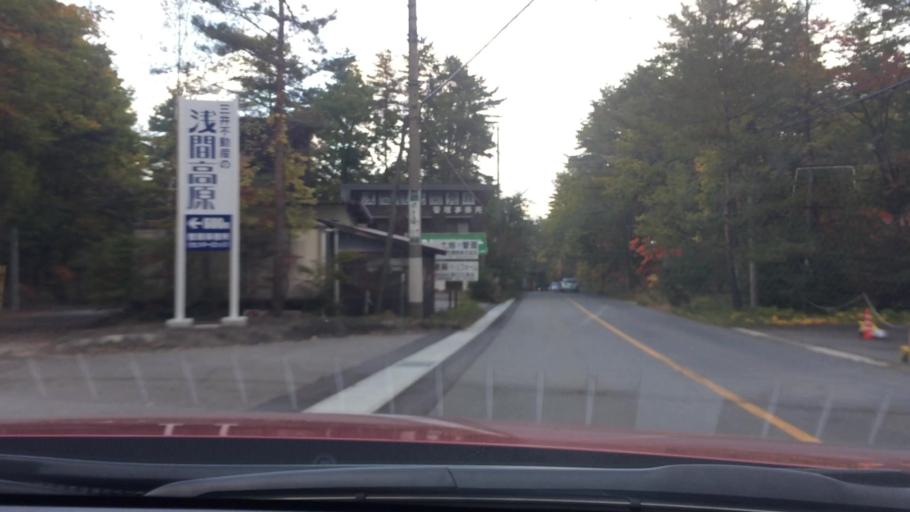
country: JP
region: Nagano
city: Komoro
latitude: 36.4393
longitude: 138.5762
